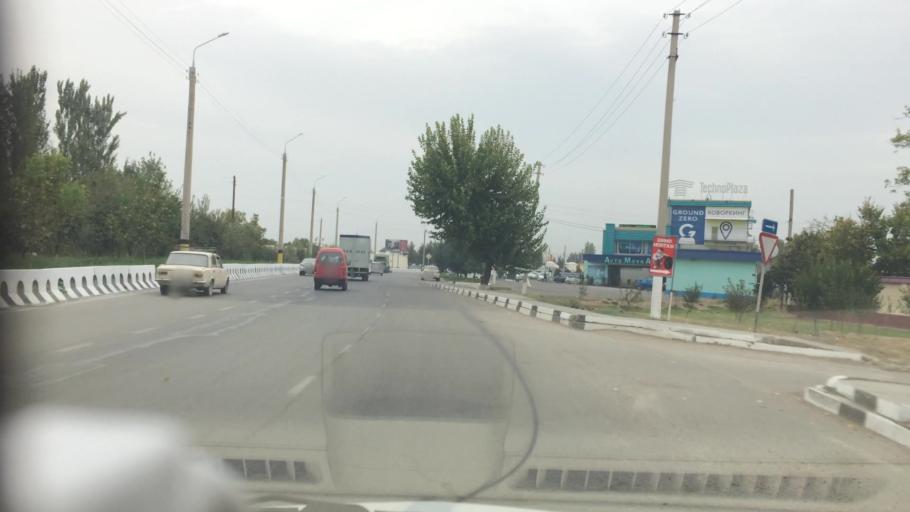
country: UZ
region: Toshkent
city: Salor
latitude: 41.3079
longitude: 69.3431
